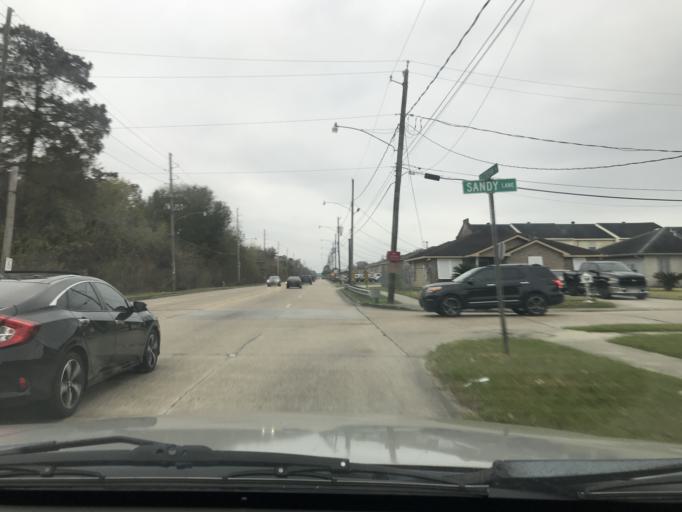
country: US
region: Louisiana
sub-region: Jefferson Parish
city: Woodmere
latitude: 29.8645
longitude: -90.0739
